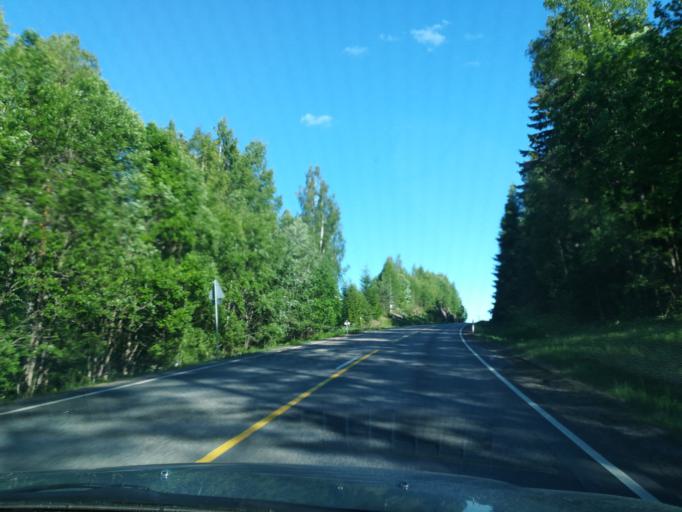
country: FI
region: South Karelia
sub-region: Imatra
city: Ruokolahti
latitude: 61.3562
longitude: 28.7179
